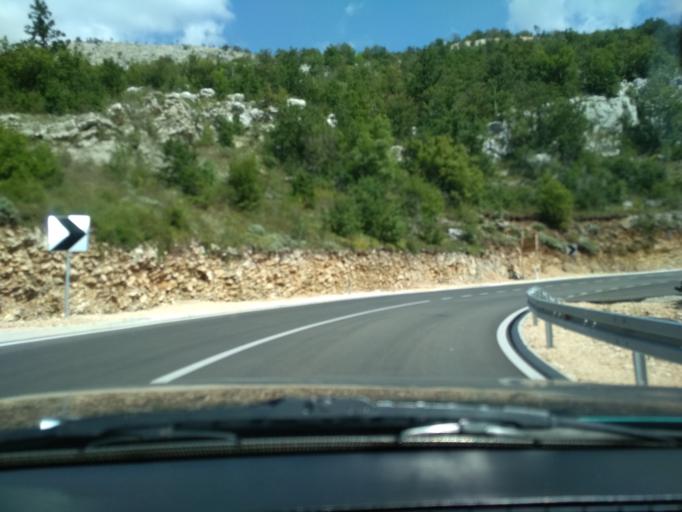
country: ME
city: Dobrota
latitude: 42.4387
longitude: 18.8313
